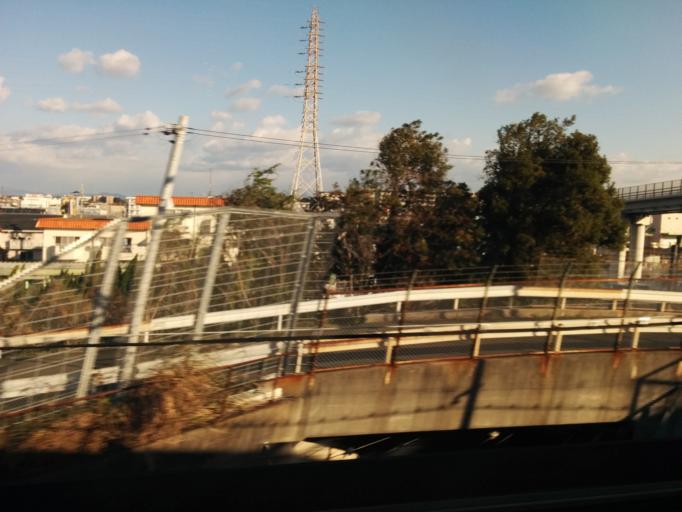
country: JP
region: Shizuoka
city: Hamamatsu
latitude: 34.6928
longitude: 137.7059
